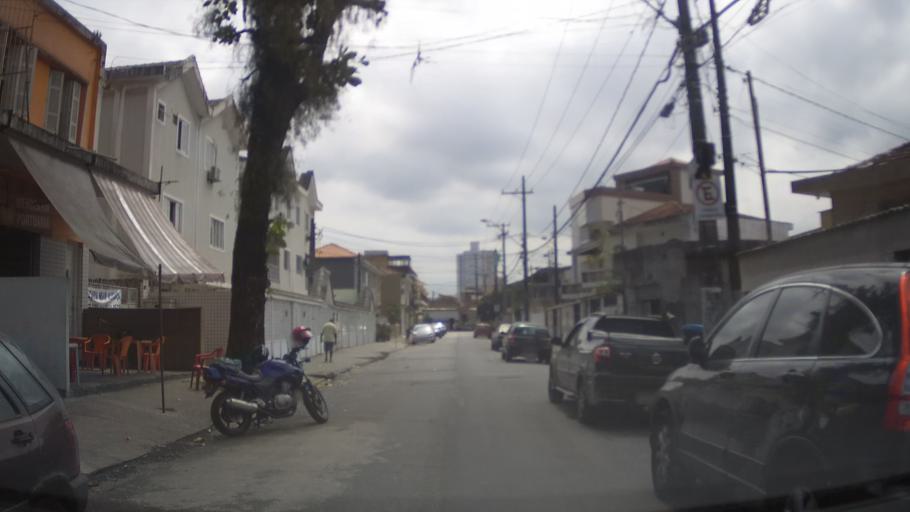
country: BR
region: Sao Paulo
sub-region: Santos
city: Santos
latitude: -23.9665
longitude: -46.3072
